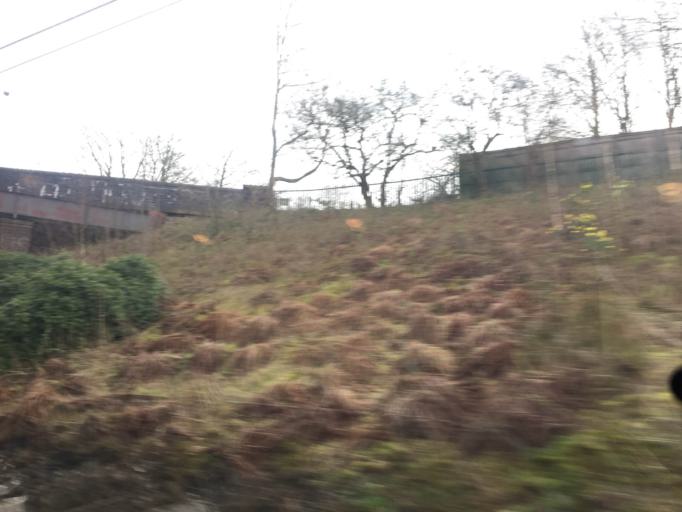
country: GB
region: England
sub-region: Borough of Wigan
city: Ince-in-Makerfield
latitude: 53.5718
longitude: -2.6398
